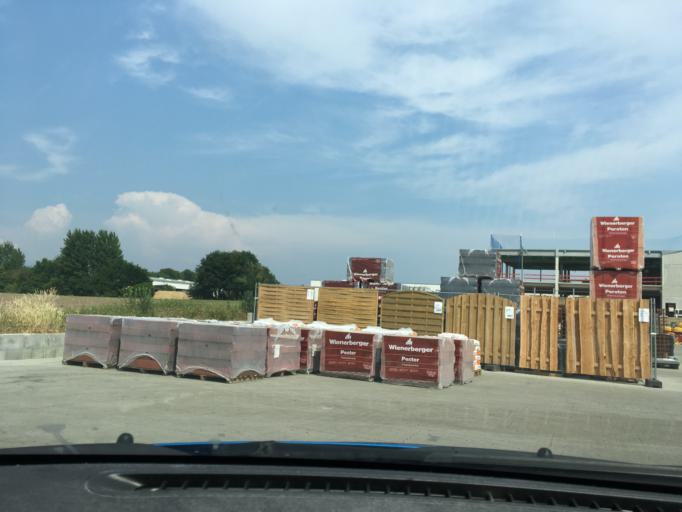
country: DE
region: Lower Saxony
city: Salzhausen
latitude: 53.2283
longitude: 10.1462
